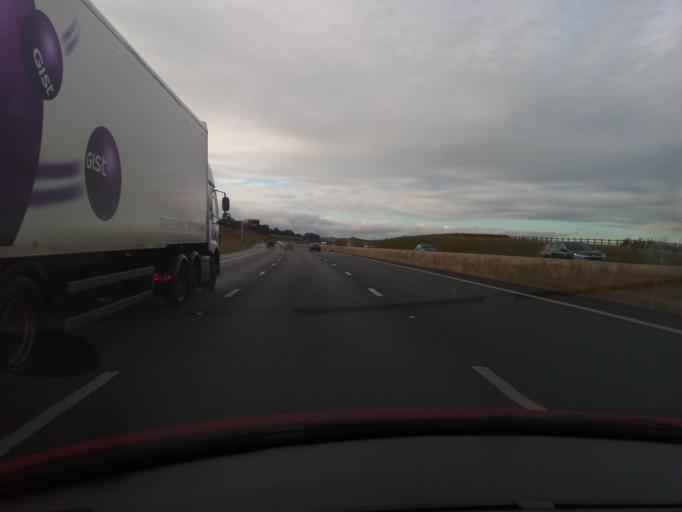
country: GB
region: England
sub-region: North Yorkshire
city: Catterick
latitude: 54.3608
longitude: -1.6226
